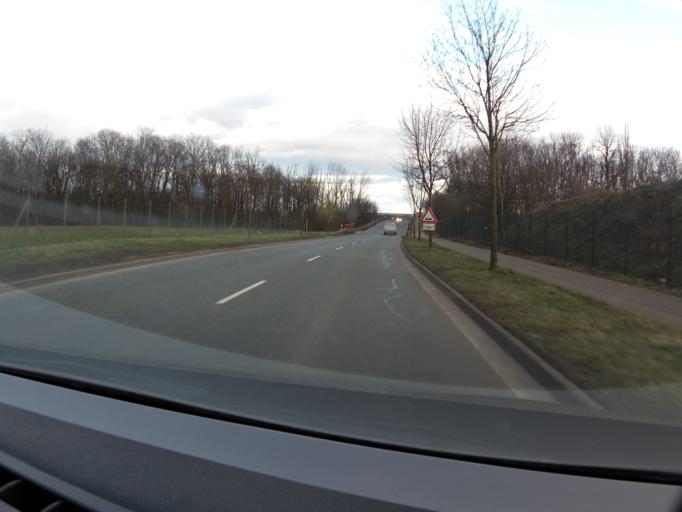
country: DE
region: Thuringia
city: Arnstadt
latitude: 50.8518
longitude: 10.9600
